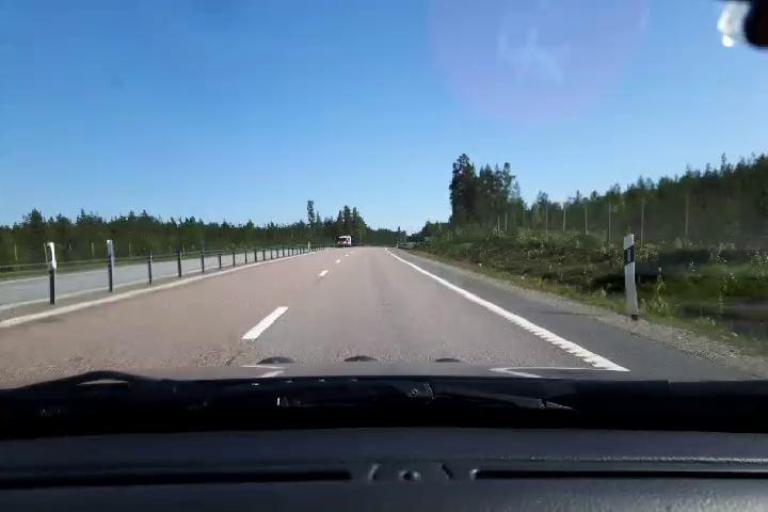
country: SE
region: Gaevleborg
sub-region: Gavle Kommun
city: Norrsundet
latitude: 60.9813
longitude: 17.0167
